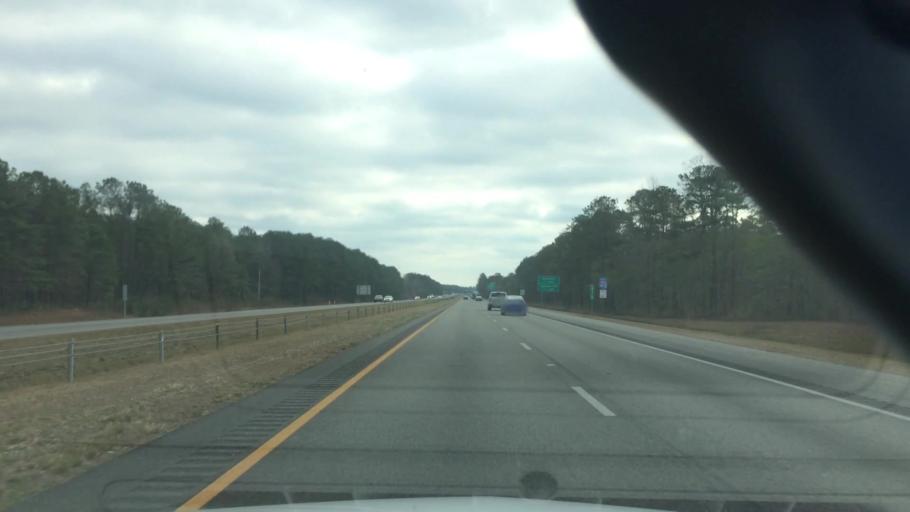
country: US
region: North Carolina
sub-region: New Hanover County
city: Skippers Corner
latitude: 34.3450
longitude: -77.8813
